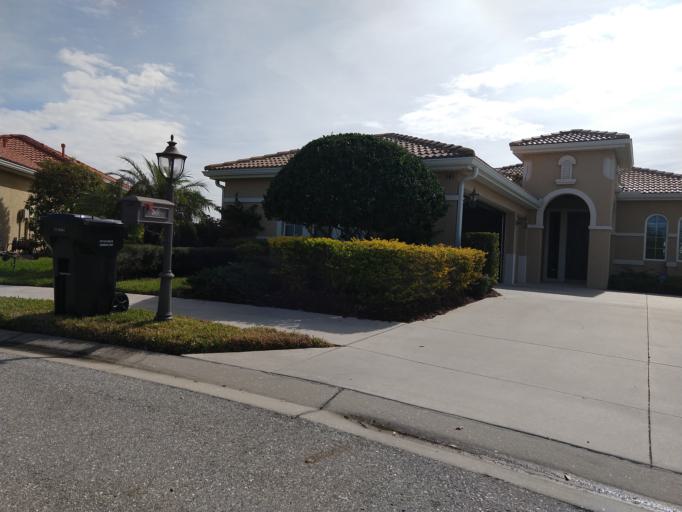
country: US
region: Florida
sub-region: Sarasota County
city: Nokomis
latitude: 27.1449
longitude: -82.3741
